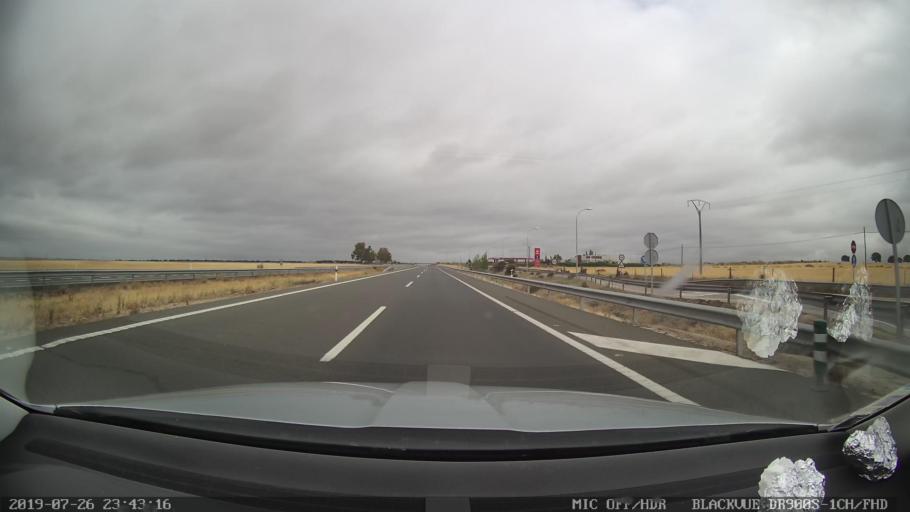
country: ES
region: Extremadura
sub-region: Provincia de Caceres
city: Trujillo
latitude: 39.5227
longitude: -5.8342
